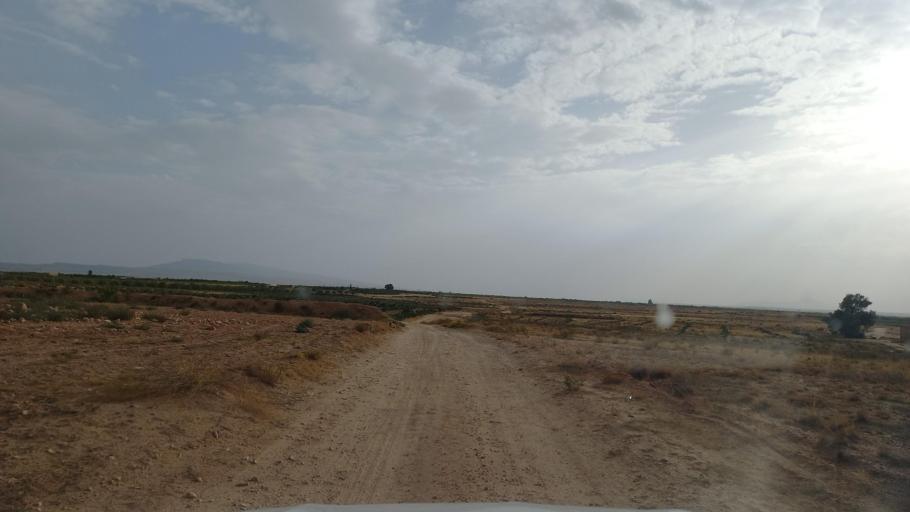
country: TN
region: Al Qasrayn
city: Kasserine
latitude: 35.2924
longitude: 9.0508
